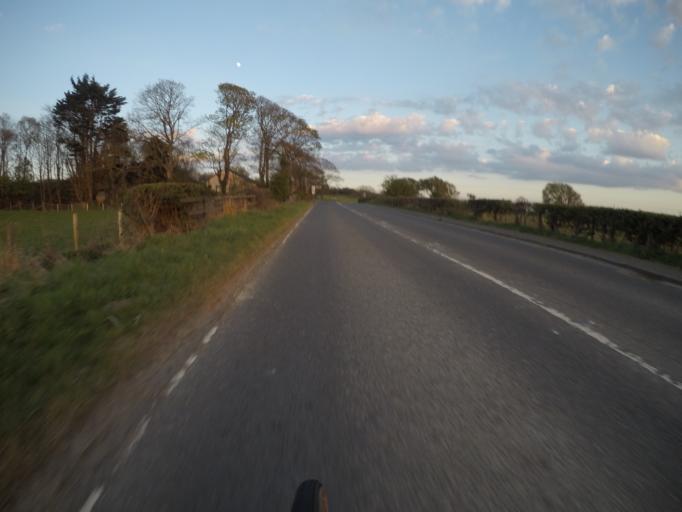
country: GB
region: Scotland
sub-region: South Ayrshire
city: Troon
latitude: 55.5566
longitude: -4.6266
